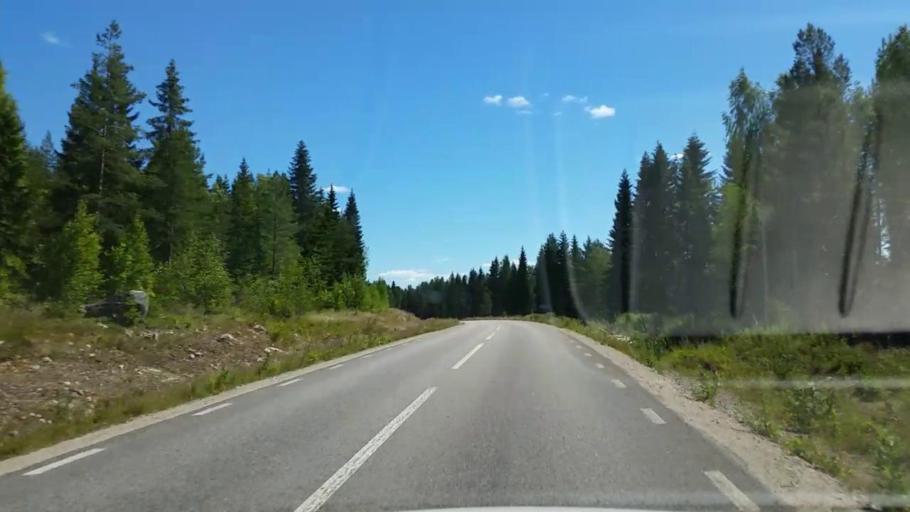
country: SE
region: Gaevleborg
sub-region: Ovanakers Kommun
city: Edsbyn
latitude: 61.5987
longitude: 15.5531
